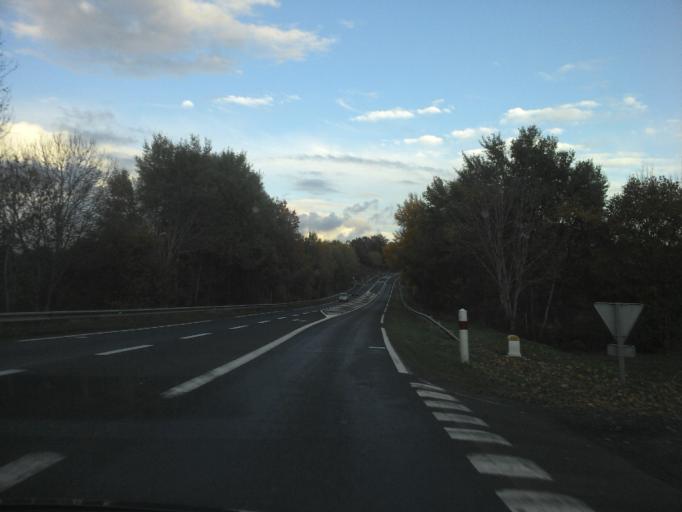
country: FR
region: Auvergne
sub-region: Departement du Puy-de-Dome
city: Gelles
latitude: 45.8448
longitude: 2.7830
